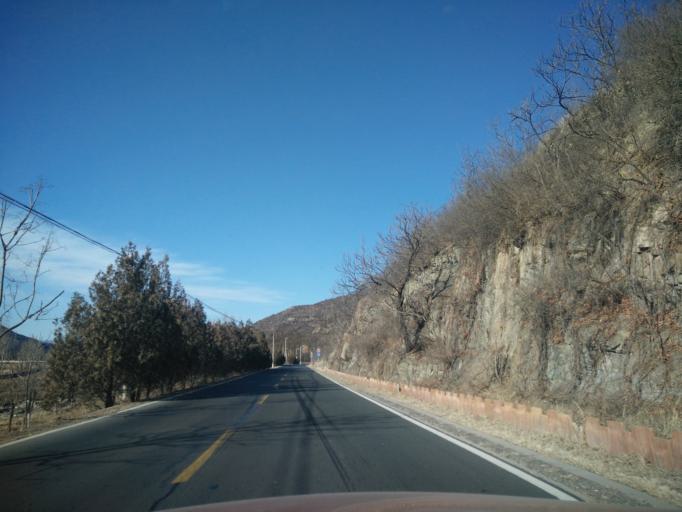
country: CN
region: Beijing
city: Zhaitang
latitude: 39.9855
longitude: 115.7289
